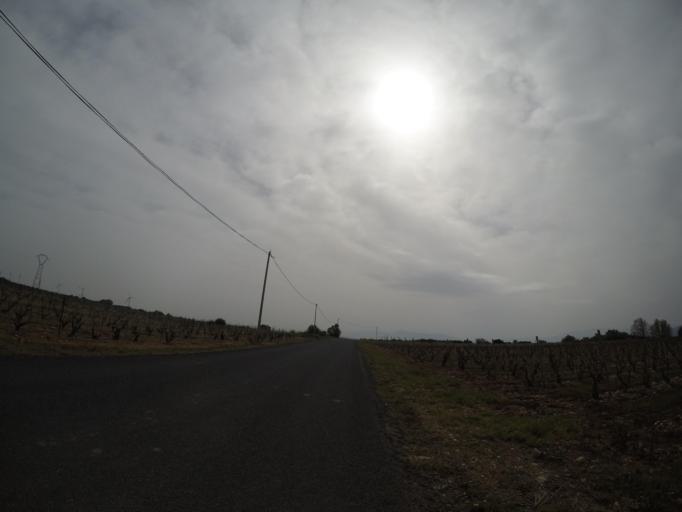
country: FR
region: Languedoc-Roussillon
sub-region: Departement des Pyrenees-Orientales
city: Pezilla-la-Riviere
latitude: 42.7132
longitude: 2.7567
